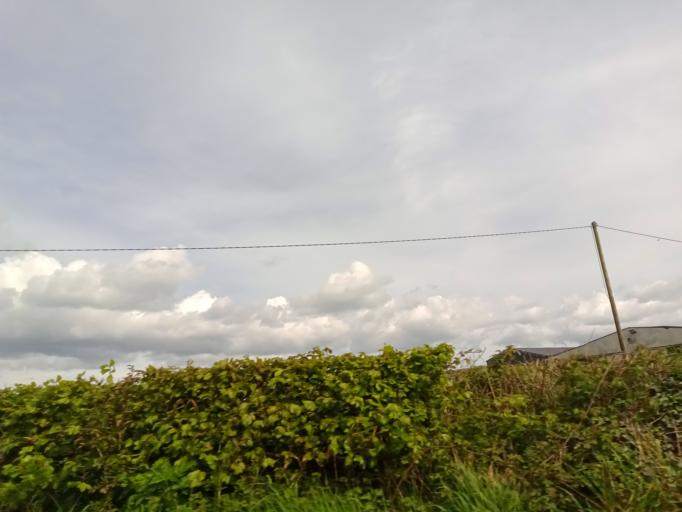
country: IE
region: Munster
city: Thurles
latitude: 52.6189
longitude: -7.7890
